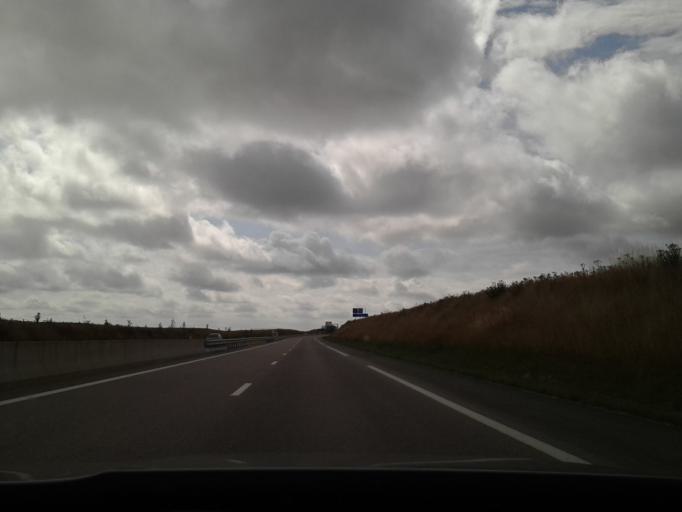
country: FR
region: Lower Normandy
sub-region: Departement de l'Orne
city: Courteilles
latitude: 48.8287
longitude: -0.1424
